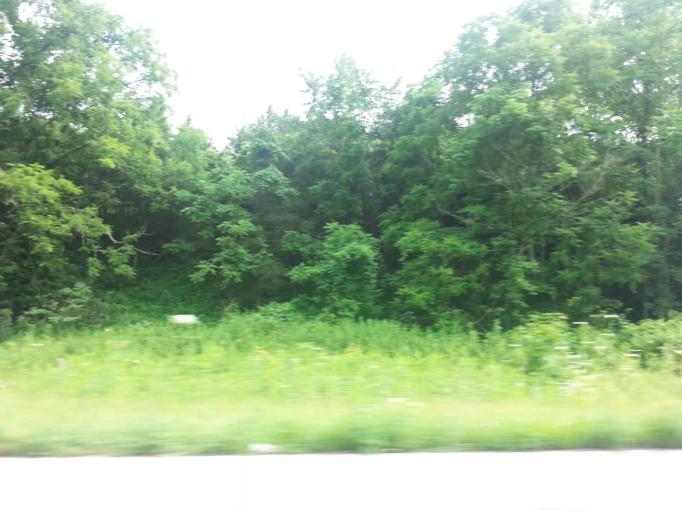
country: US
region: Kentucky
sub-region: Robertson County
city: Mount Olivet
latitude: 38.5251
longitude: -84.1716
